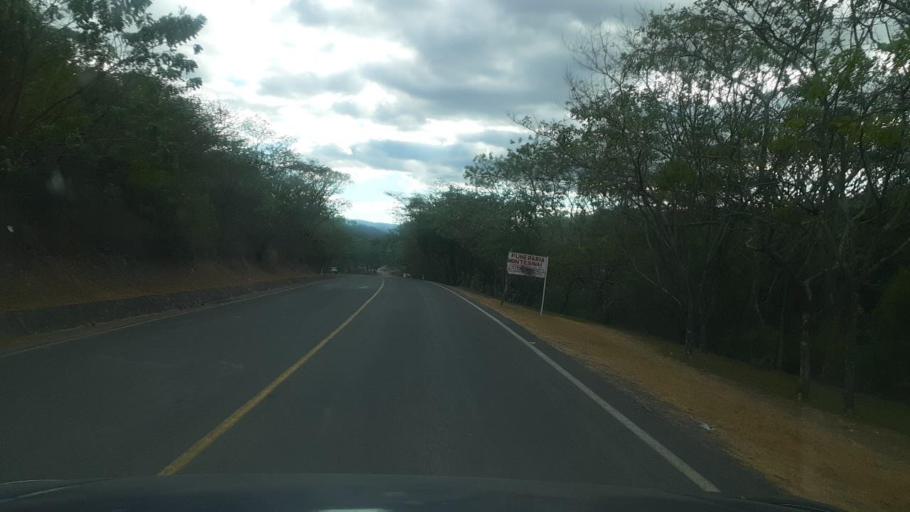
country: NI
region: Madriz
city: Somoto
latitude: 13.5021
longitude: -86.5709
